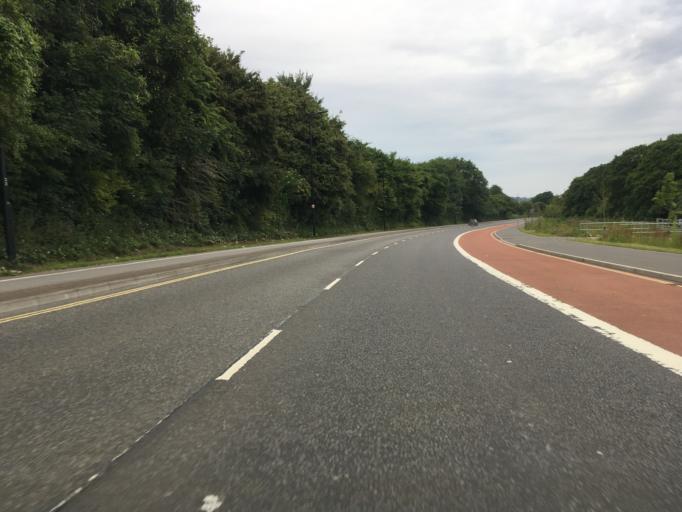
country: GB
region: England
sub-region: Bristol
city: Bristol
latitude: 51.4216
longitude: -2.6041
